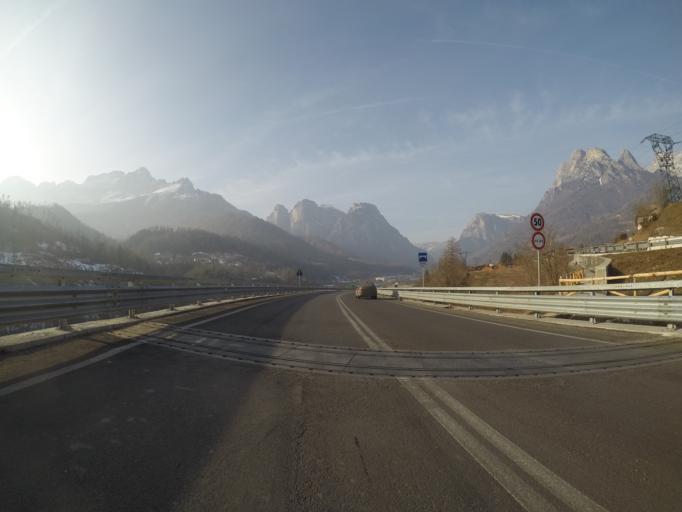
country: IT
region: Veneto
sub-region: Provincia di Belluno
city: Agordo
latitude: 46.2716
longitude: 12.0364
